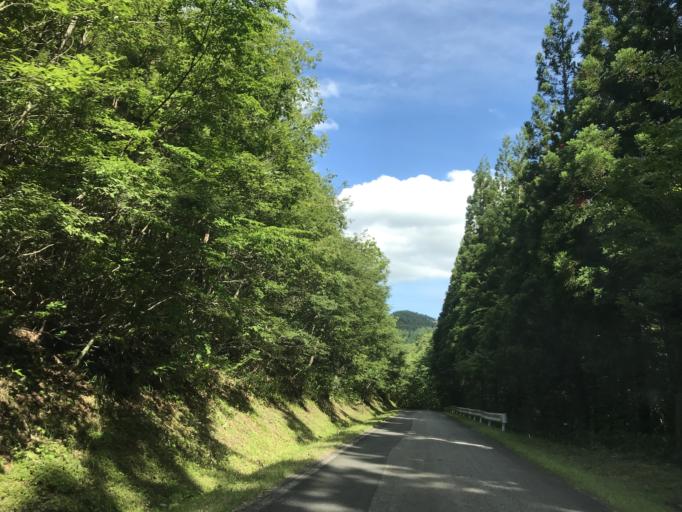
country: JP
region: Iwate
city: Ichinoseki
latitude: 38.9259
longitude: 140.9369
